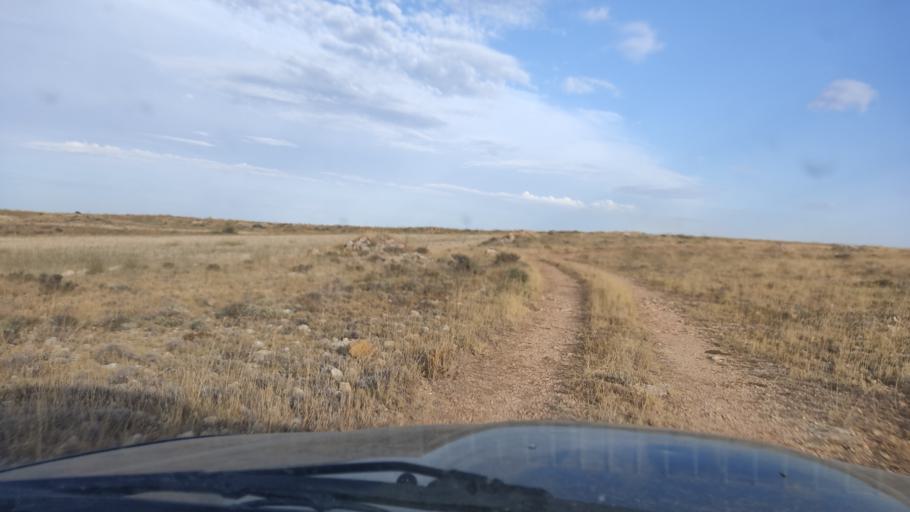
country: ES
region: Aragon
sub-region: Provincia de Teruel
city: Monforte de Moyuela
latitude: 41.0619
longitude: -0.9724
